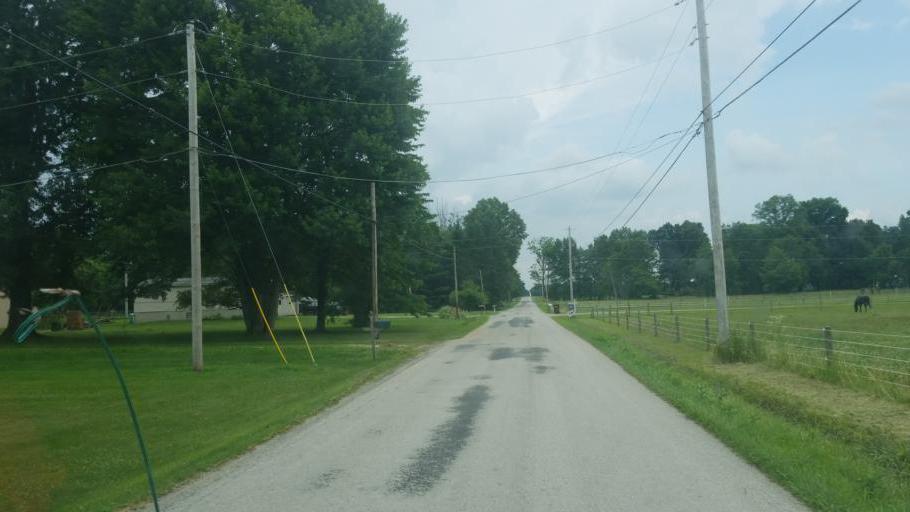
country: US
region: Ohio
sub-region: Wayne County
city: Wooster
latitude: 40.8945
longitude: -81.9474
